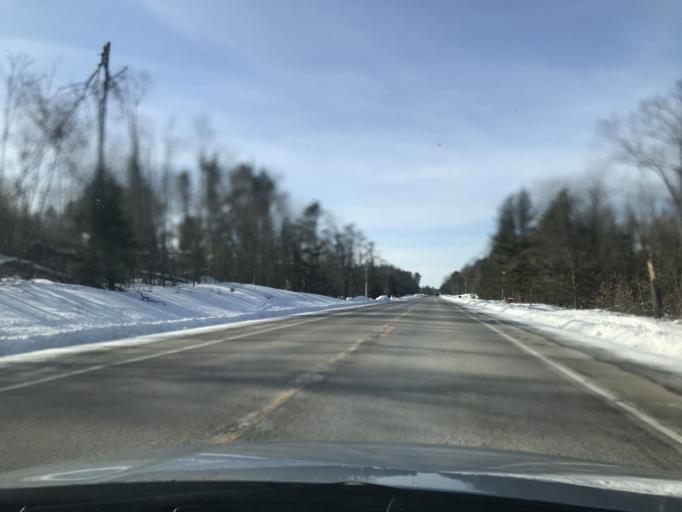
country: US
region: Wisconsin
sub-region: Oconto County
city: Gillett
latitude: 45.1287
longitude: -88.4131
